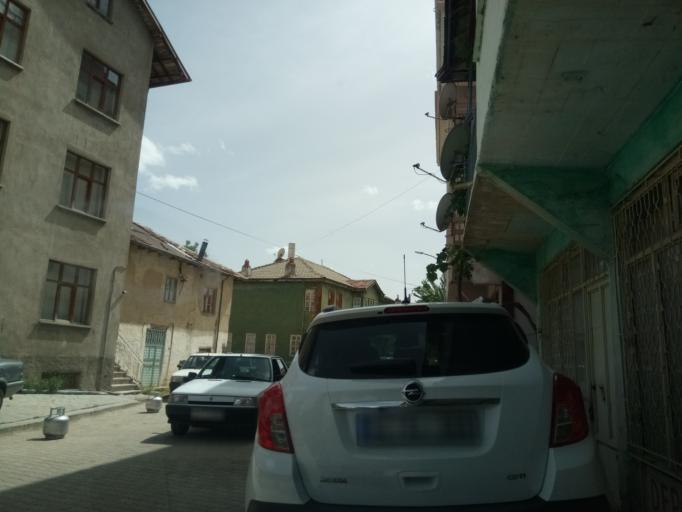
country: TR
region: Konya
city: Bozkir
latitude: 37.1905
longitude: 32.2429
